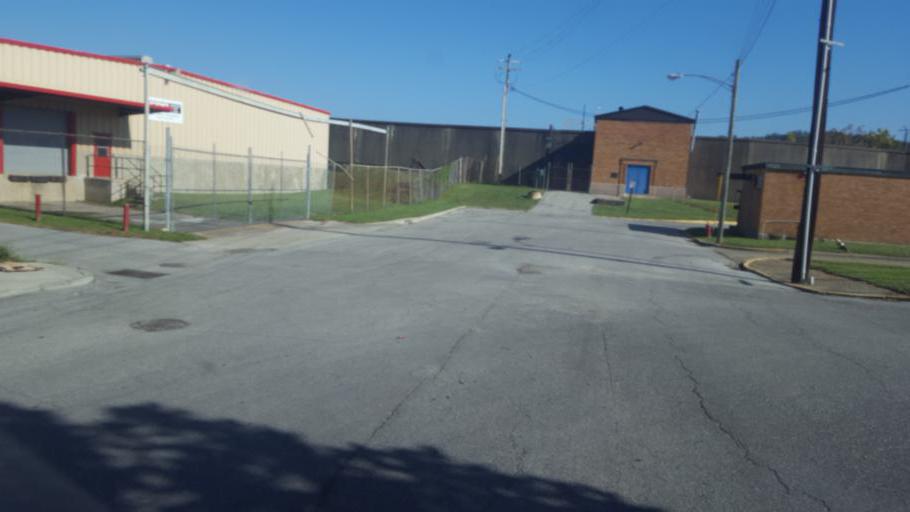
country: US
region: Ohio
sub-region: Brown County
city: Aberdeen
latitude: 38.6497
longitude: -83.7680
